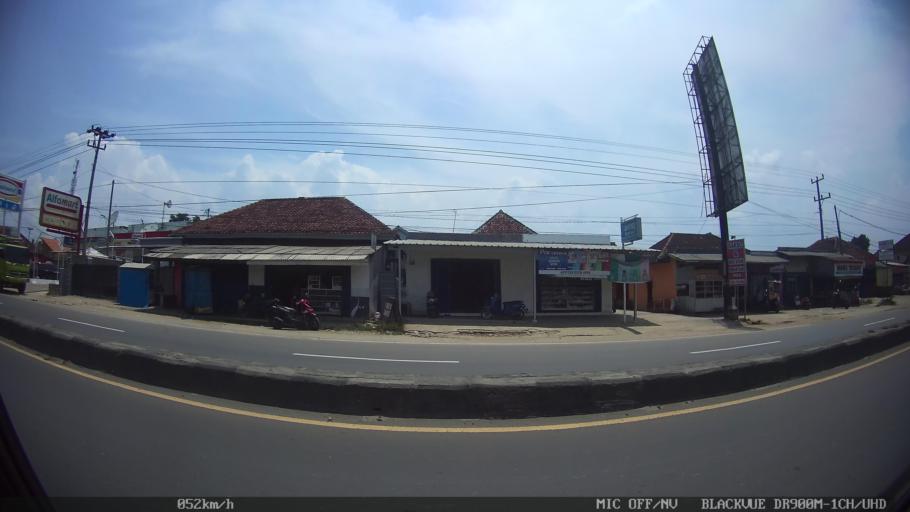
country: ID
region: Lampung
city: Natar
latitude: -5.3237
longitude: 105.1999
